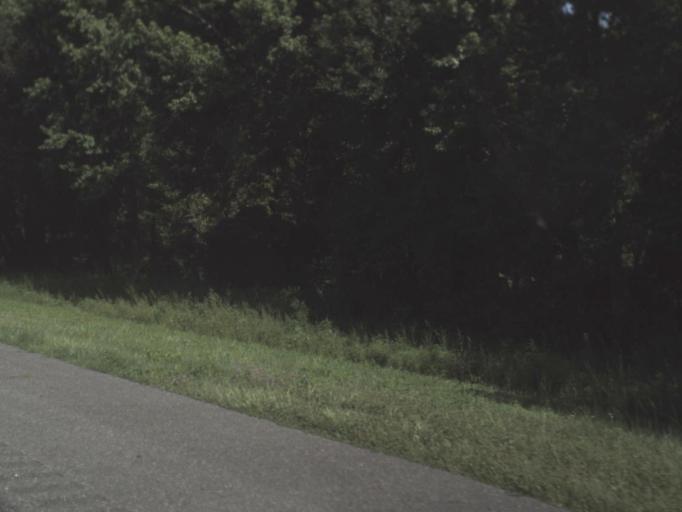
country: US
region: Florida
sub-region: Suwannee County
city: Wellborn
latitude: 30.2915
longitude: -82.8737
